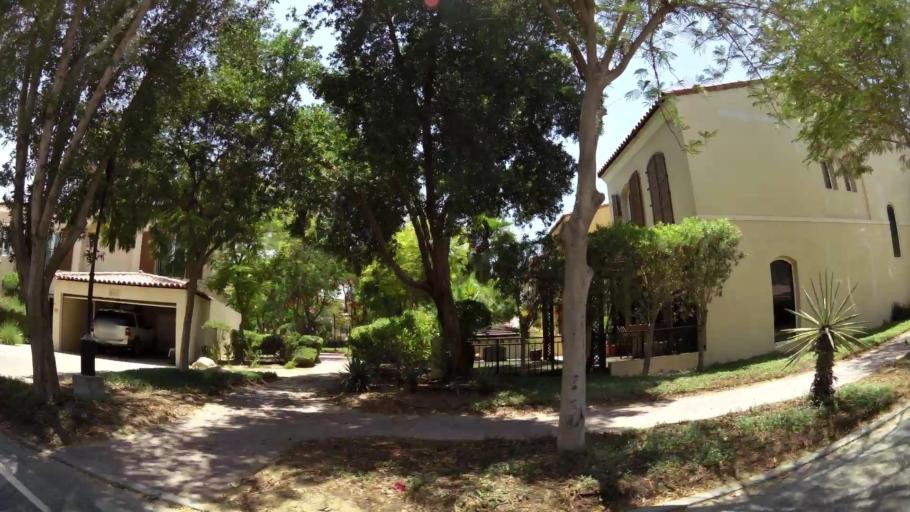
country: AE
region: Dubai
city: Dubai
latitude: 25.0076
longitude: 55.1609
